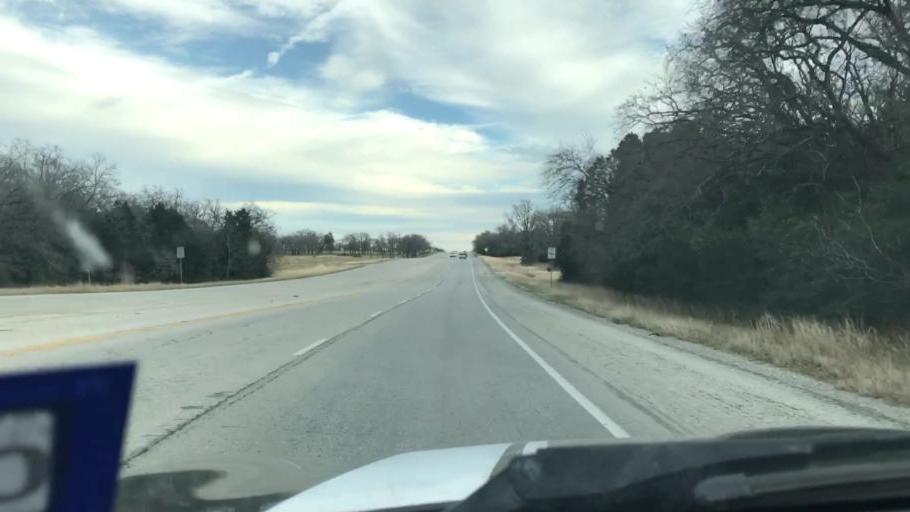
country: US
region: Texas
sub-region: Bastrop County
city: Camp Swift
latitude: 30.2930
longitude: -97.2564
